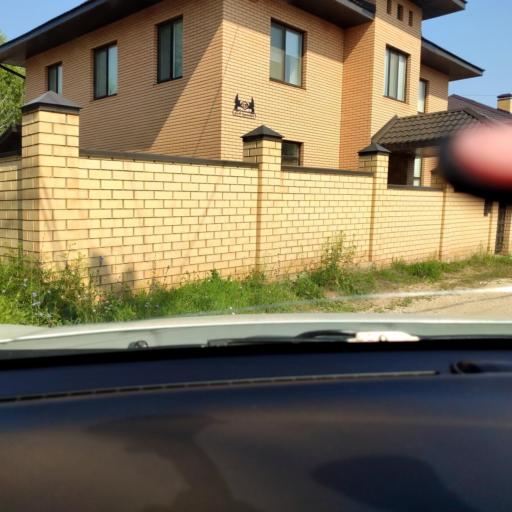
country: RU
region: Tatarstan
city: Stolbishchi
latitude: 55.7382
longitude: 49.2537
